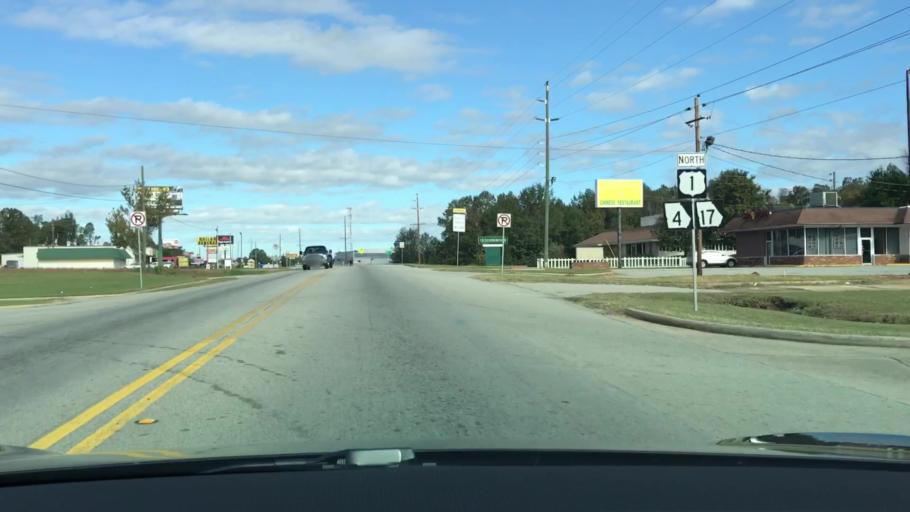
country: US
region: Georgia
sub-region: Jefferson County
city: Louisville
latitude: 33.0045
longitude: -82.3959
